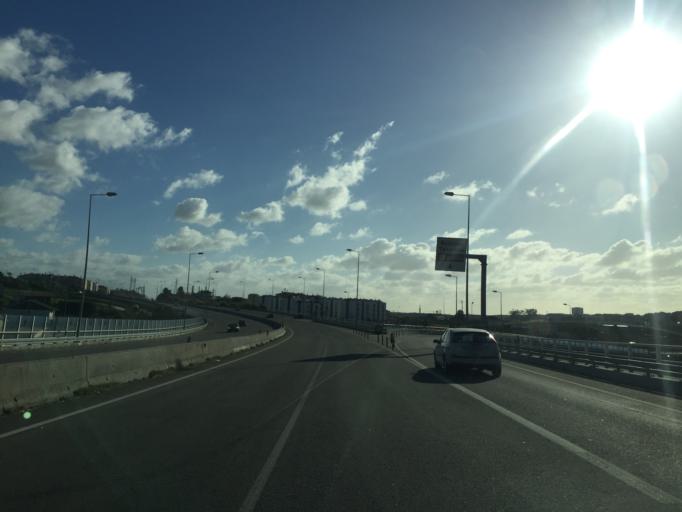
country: PT
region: Coimbra
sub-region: Figueira da Foz
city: Tavarede
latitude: 40.1662
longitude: -8.8398
